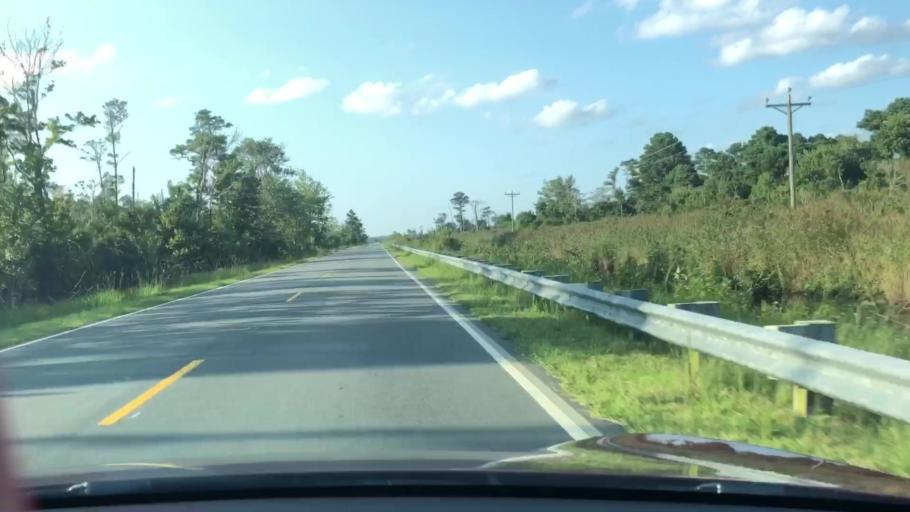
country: US
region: North Carolina
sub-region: Dare County
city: Wanchese
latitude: 35.6761
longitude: -75.7793
